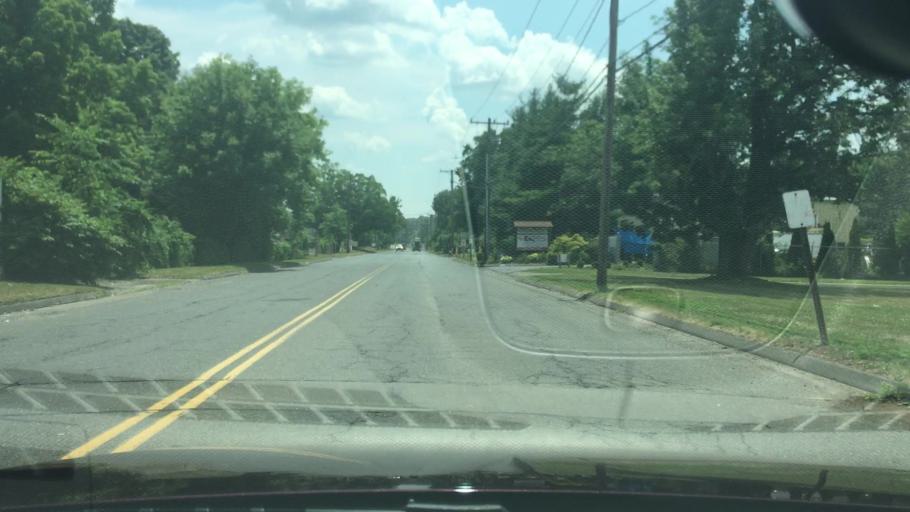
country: US
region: Connecticut
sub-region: Hartford County
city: Kensington
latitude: 41.6493
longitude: -72.7516
